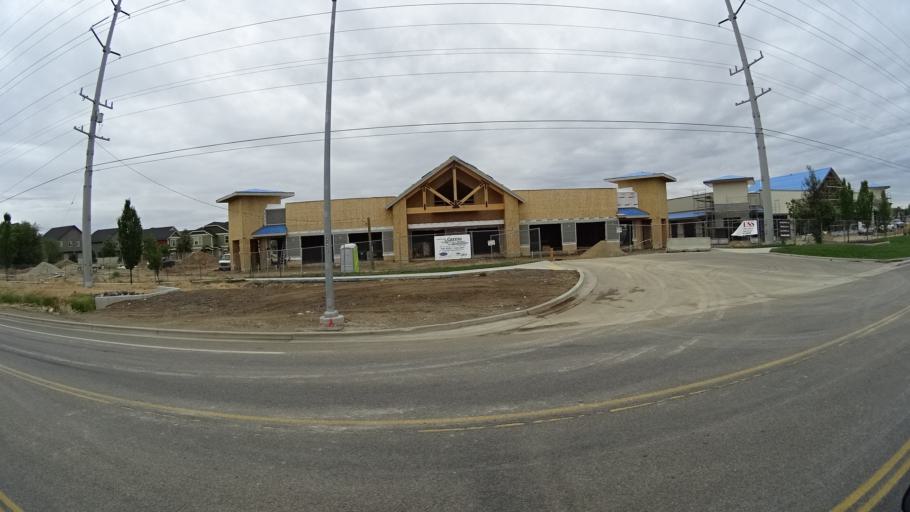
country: US
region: Idaho
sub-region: Ada County
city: Meridian
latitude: 43.6485
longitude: -116.4121
